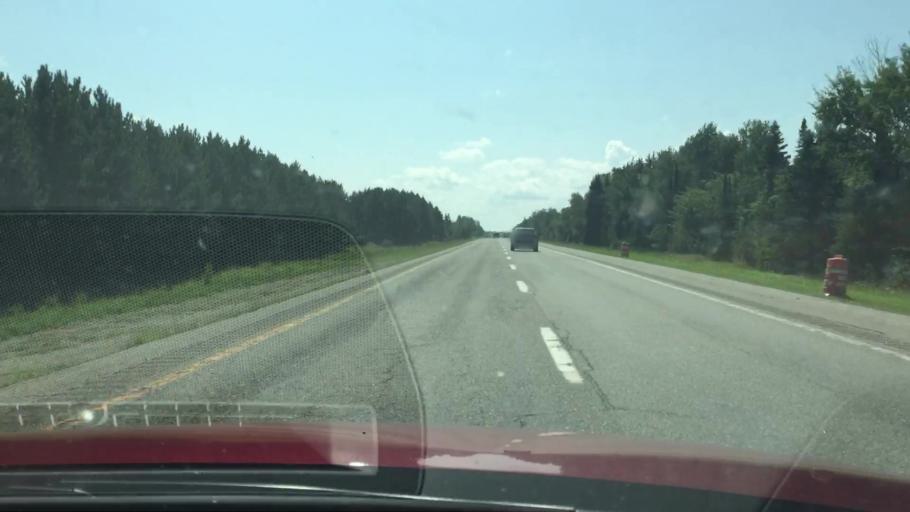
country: US
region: Maine
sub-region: Penobscot County
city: Patten
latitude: 45.8637
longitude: -68.4192
